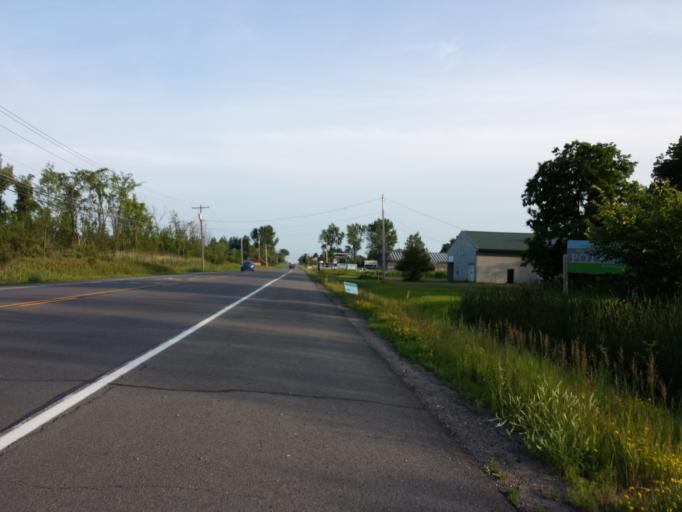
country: US
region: New York
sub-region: St. Lawrence County
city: Potsdam
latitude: 44.7049
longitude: -74.9873
